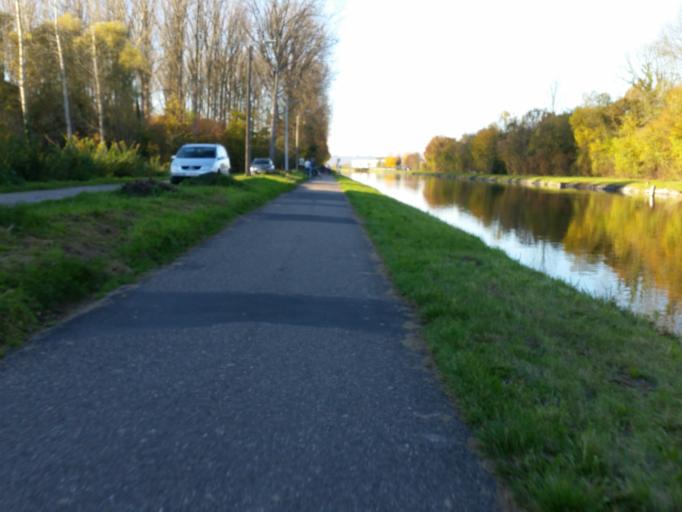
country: BE
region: Flanders
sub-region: Provincie Vlaams-Brabant
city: Herent
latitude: 50.9408
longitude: 4.6635
